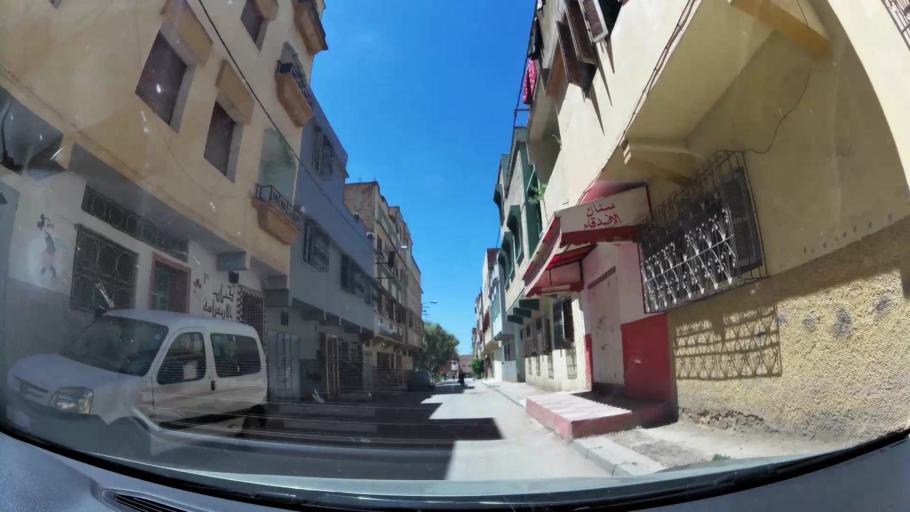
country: MA
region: Meknes-Tafilalet
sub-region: Meknes
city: Meknes
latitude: 33.9060
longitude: -5.5779
